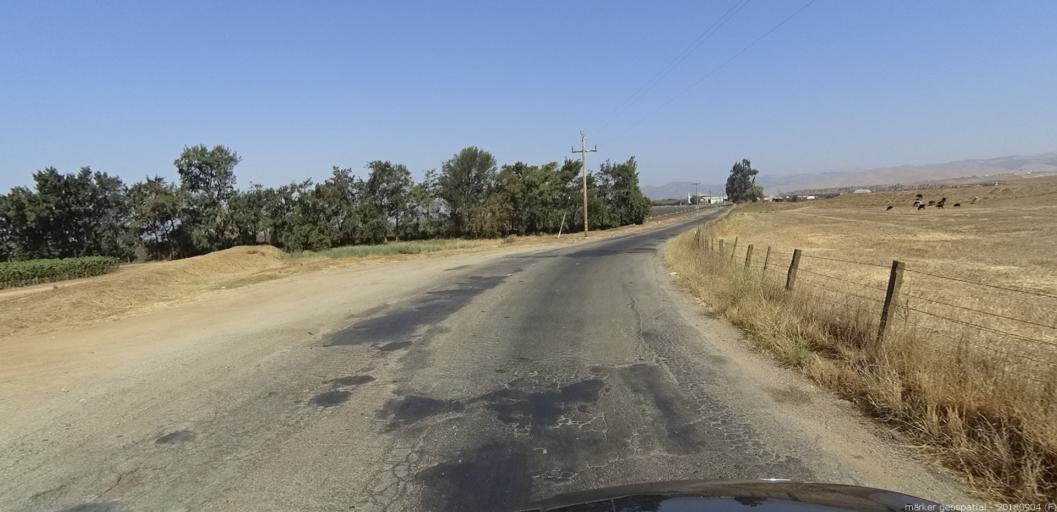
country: US
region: California
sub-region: Monterey County
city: Gonzales
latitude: 36.5148
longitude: -121.4113
